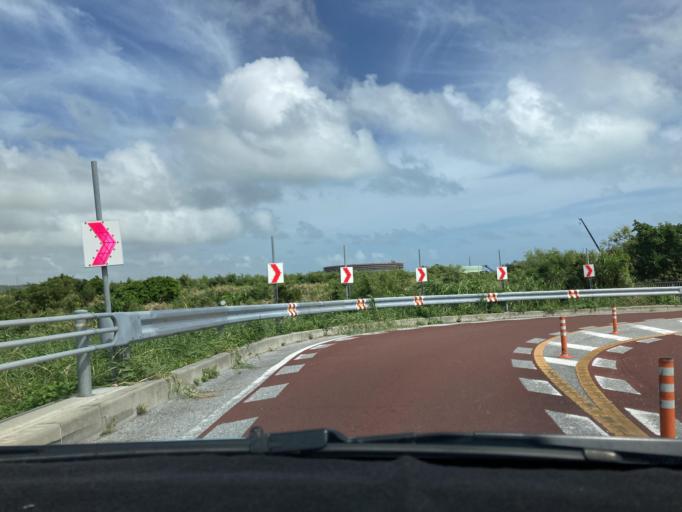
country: JP
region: Okinawa
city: Ginowan
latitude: 26.2179
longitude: 127.7733
